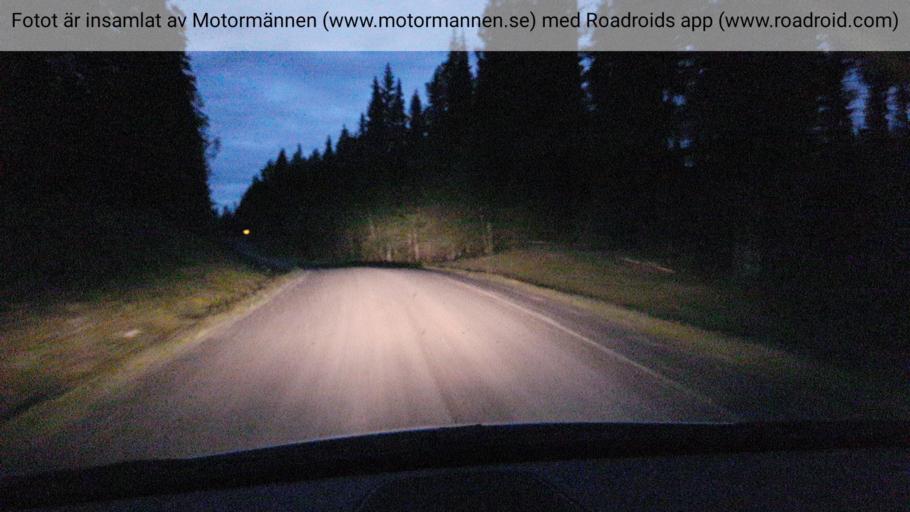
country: SE
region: Jaemtland
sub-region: Braecke Kommun
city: Braecke
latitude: 63.2744
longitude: 15.3759
